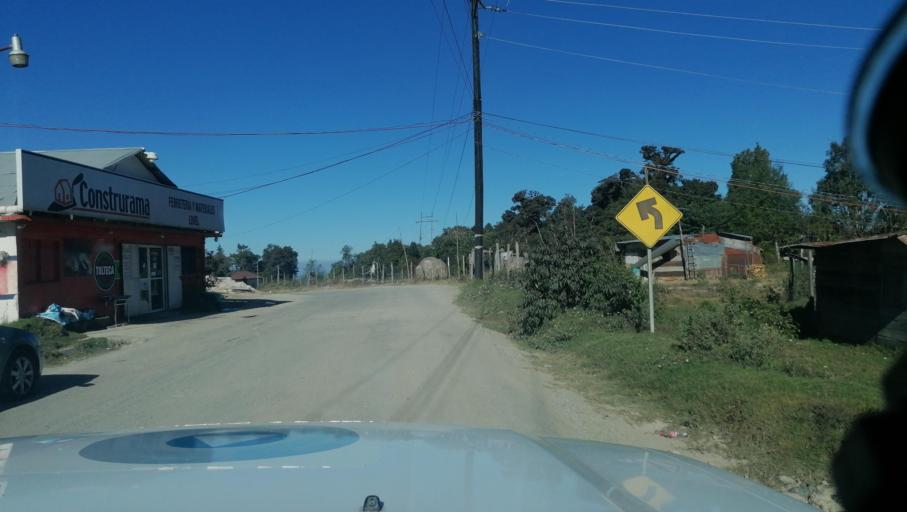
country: MX
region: Chiapas
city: Motozintla de Mendoza
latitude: 15.2630
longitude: -92.2167
